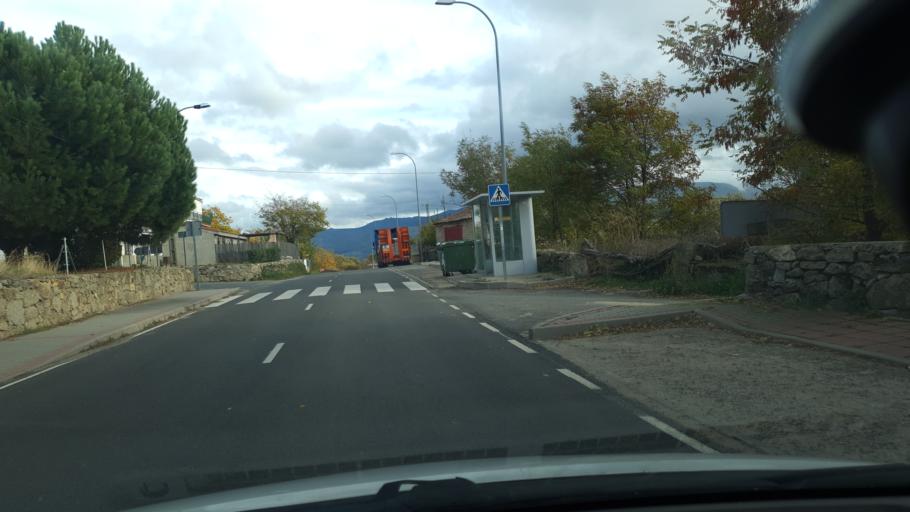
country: ES
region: Castille and Leon
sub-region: Provincia de Avila
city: Hoyocasero
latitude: 40.3978
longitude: -4.9758
